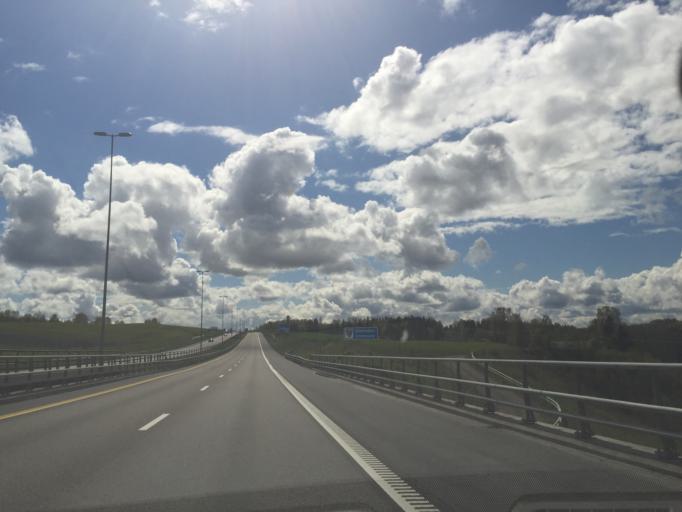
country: NO
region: Akershus
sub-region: Eidsvoll
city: Raholt
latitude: 60.2404
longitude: 11.1789
